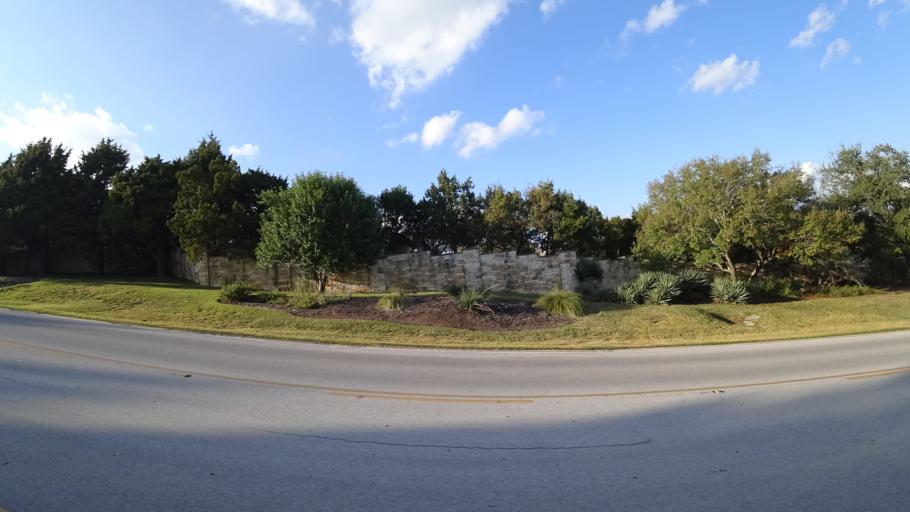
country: US
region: Texas
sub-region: Travis County
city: Barton Creek
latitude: 30.2956
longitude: -97.8597
